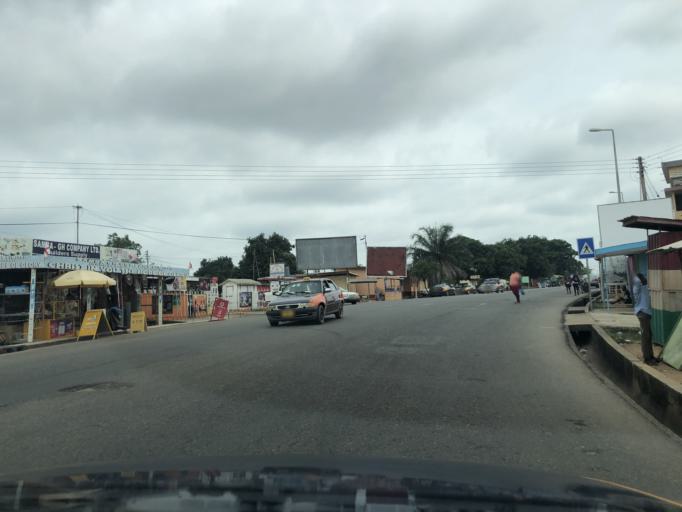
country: GH
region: Eastern
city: Koforidua
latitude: 6.1022
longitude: -0.2664
